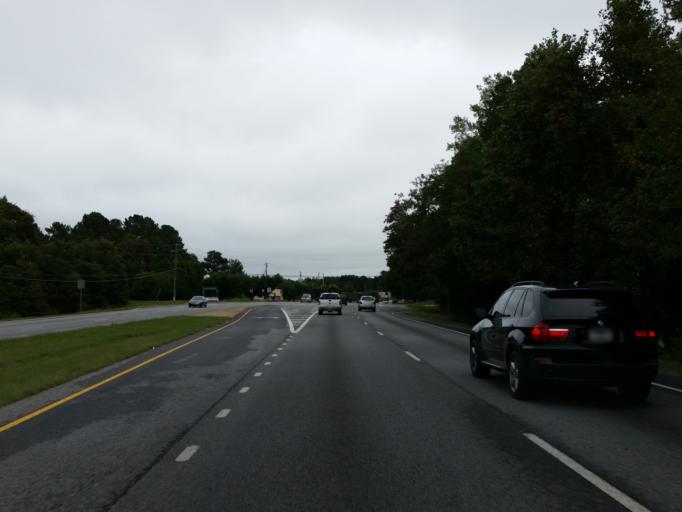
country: US
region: Georgia
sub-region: Clayton County
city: Irondale
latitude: 33.4976
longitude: -84.3453
